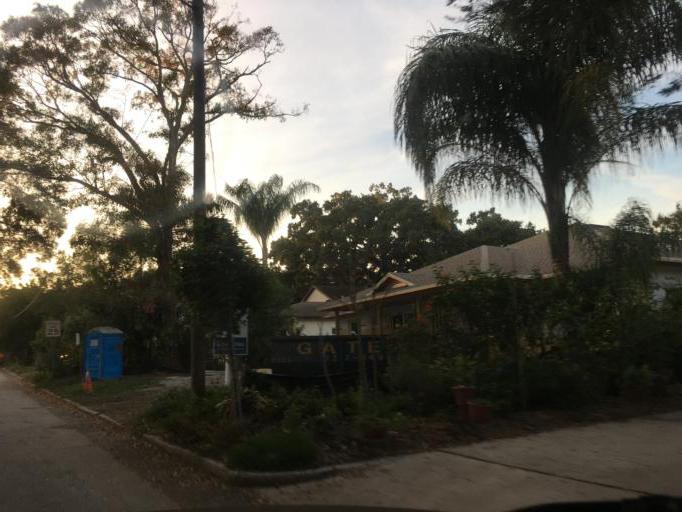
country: US
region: Florida
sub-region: Pinellas County
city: Saint Petersburg
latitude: 27.7940
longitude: -82.6348
